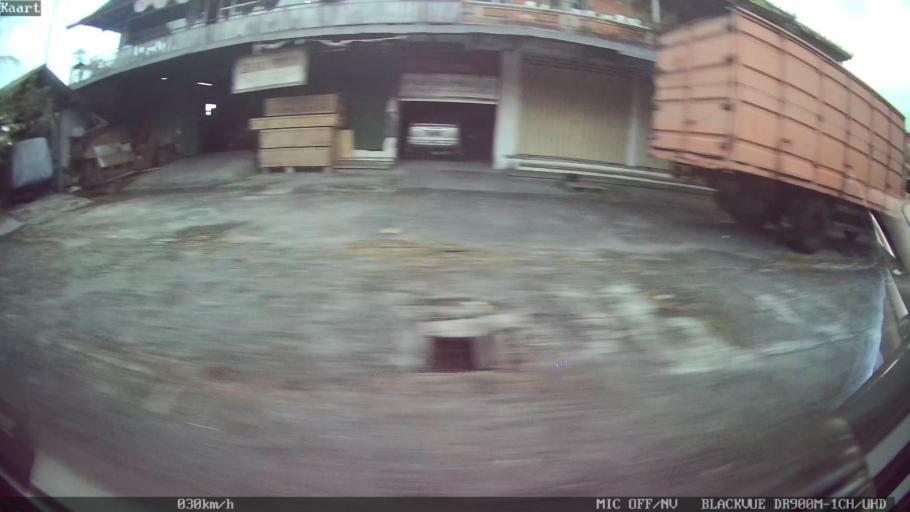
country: ID
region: Bali
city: Banjar Sedang
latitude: -8.5626
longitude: 115.2343
